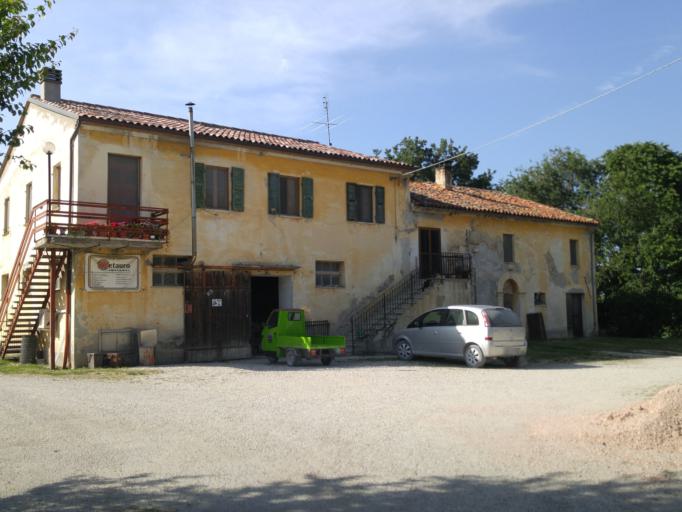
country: IT
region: The Marches
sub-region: Provincia di Pesaro e Urbino
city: Tavernelle
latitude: 43.7254
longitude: 12.9004
